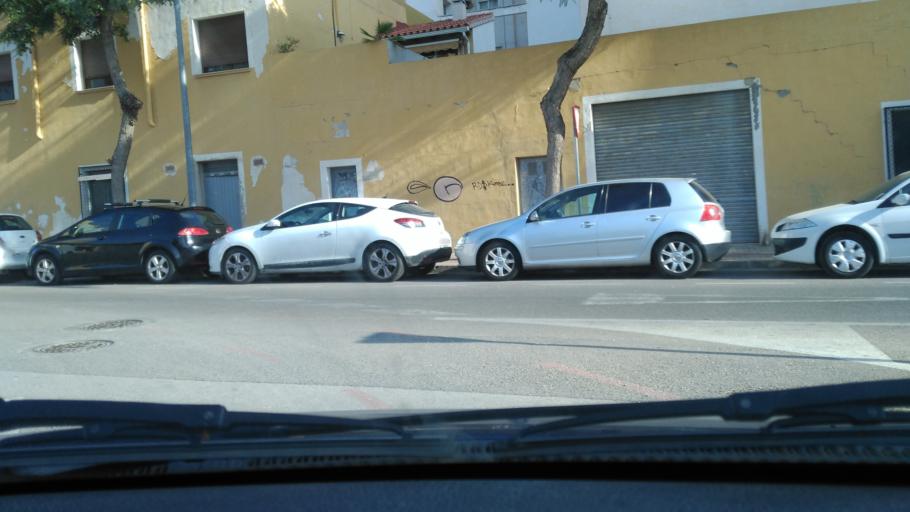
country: ES
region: Valencia
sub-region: Provincia de Alicante
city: Denia
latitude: 38.8375
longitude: 0.1010
